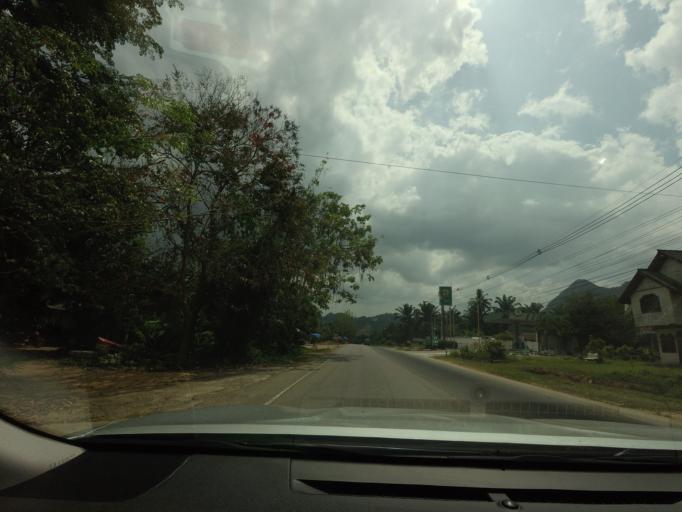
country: TH
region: Phangnga
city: Ban Ao Nang
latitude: 8.0992
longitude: 98.8024
